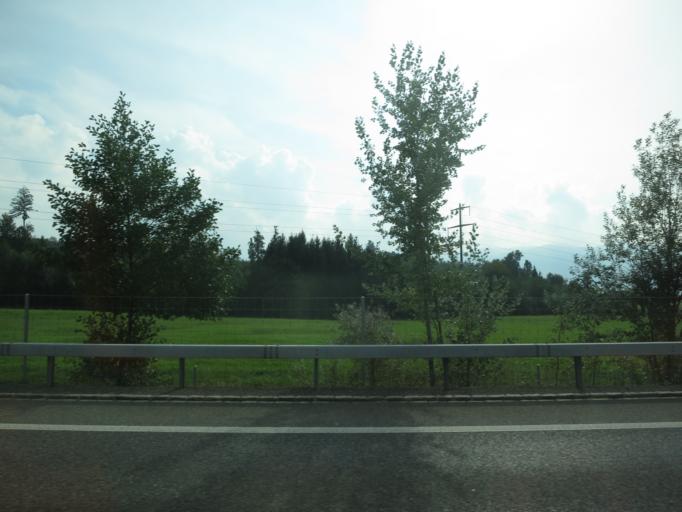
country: CH
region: Zurich
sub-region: Bezirk Hinwil
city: Rueti / Dorfzentrum, Suedl. Teil
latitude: 47.2270
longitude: 8.8784
